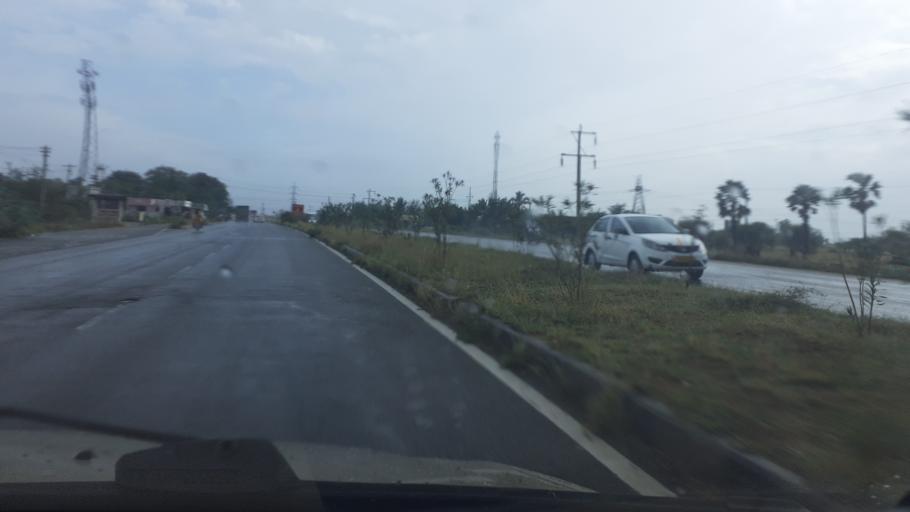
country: IN
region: Tamil Nadu
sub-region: Tirunelveli Kattabo
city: Gangaikondan
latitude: 8.8988
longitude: 77.7650
